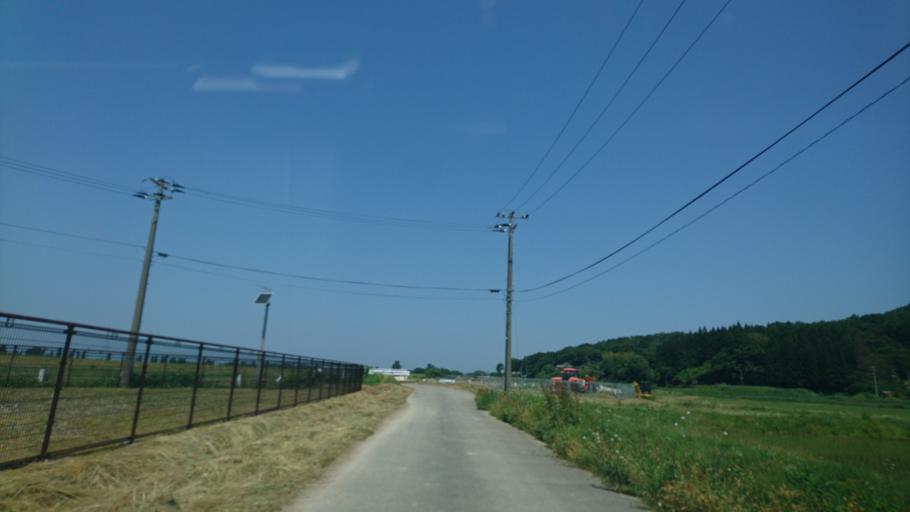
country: JP
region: Niigata
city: Murakami
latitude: 38.1243
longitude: 139.4754
